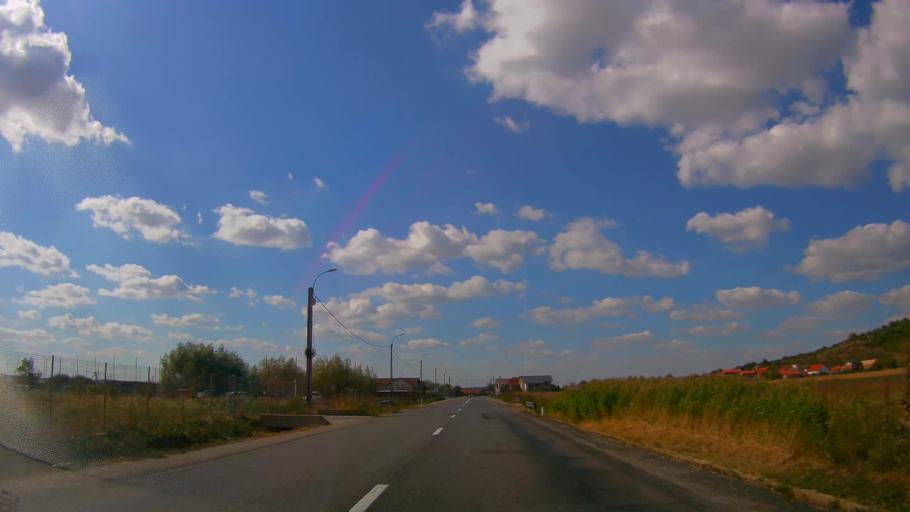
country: RO
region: Salaj
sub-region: Comuna Sarmasag
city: Sarmasag
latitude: 47.3365
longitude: 22.8419
